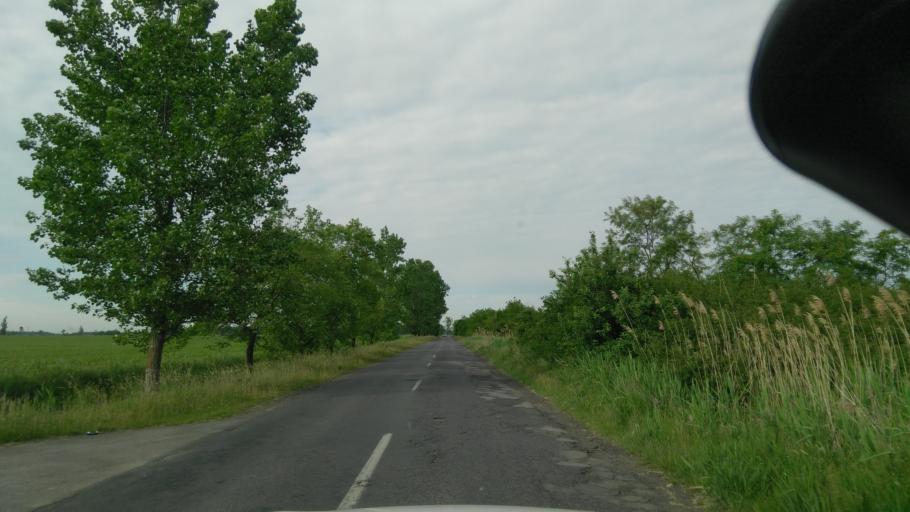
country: HU
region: Bekes
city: Ketegyhaza
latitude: 46.5702
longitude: 21.2124
